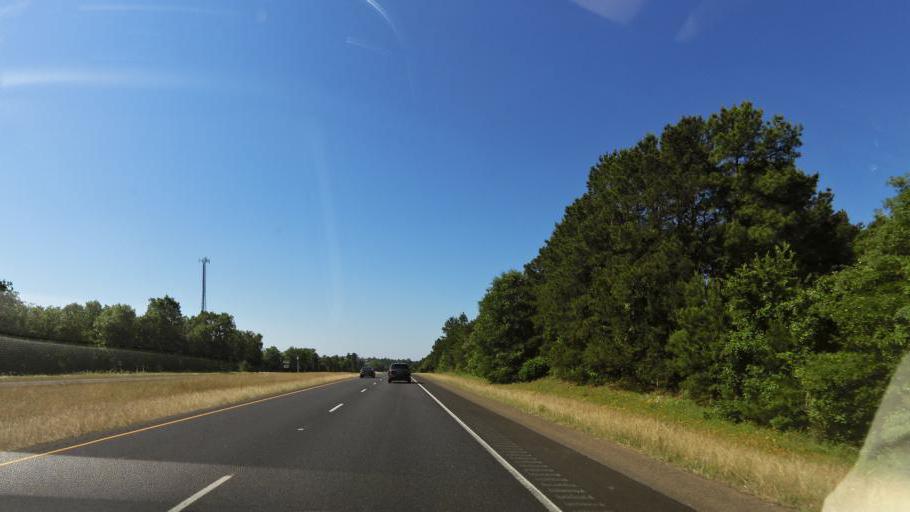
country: US
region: Texas
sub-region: Nacogdoches County
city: Nacogdoches
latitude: 31.5303
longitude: -94.6947
